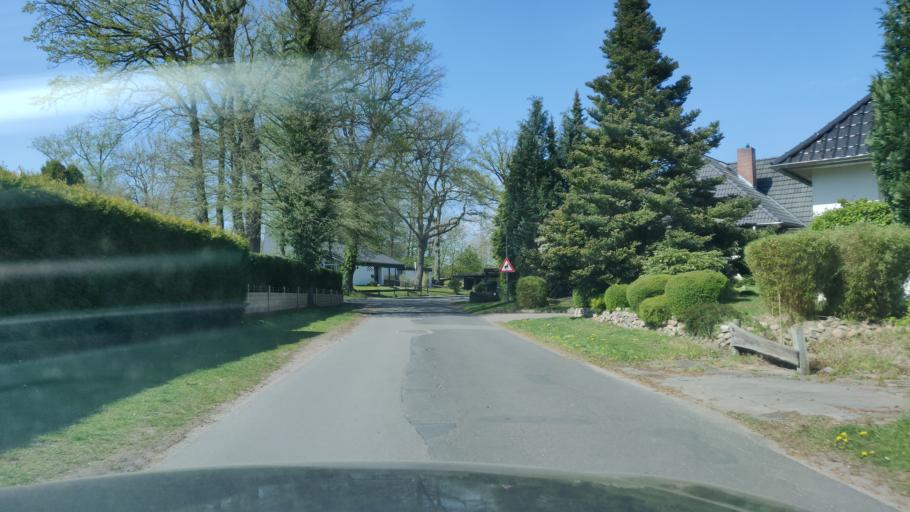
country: DE
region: Lower Saxony
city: Harmstorf
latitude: 53.3742
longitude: 9.9946
